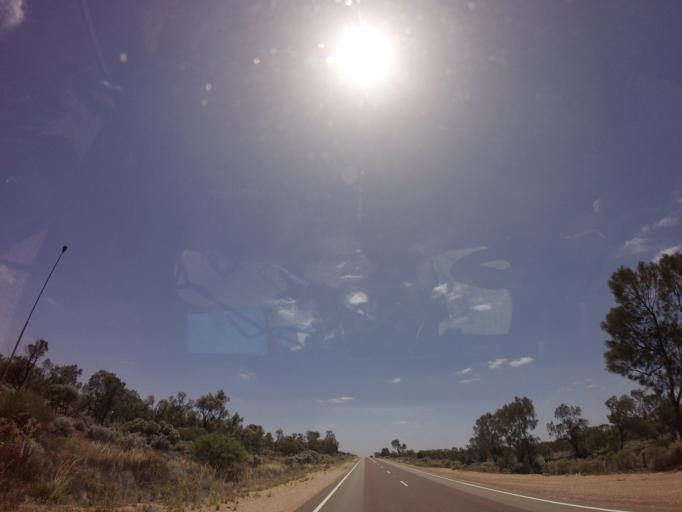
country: AU
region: South Australia
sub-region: Whyalla
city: Whyalla
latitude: -32.8289
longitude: 137.0354
